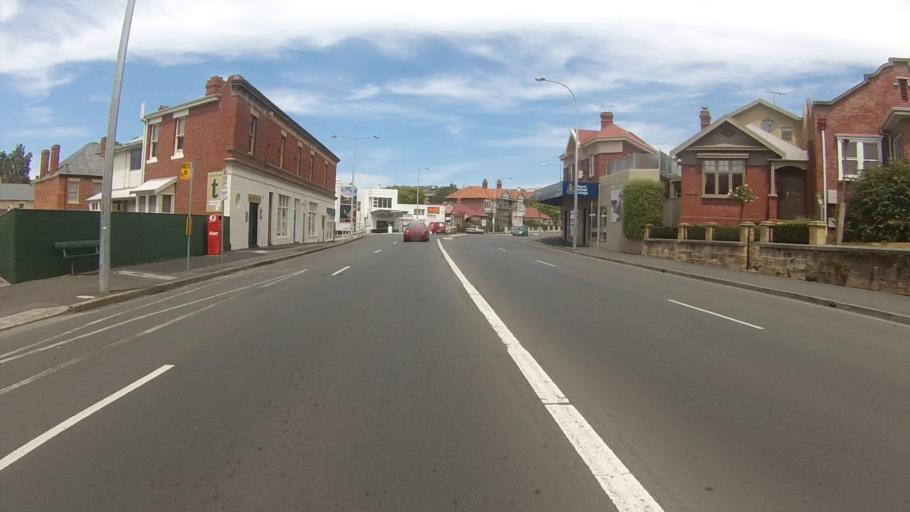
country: AU
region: Tasmania
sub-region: Hobart
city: Sandy Bay
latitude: -42.8886
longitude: 147.3302
